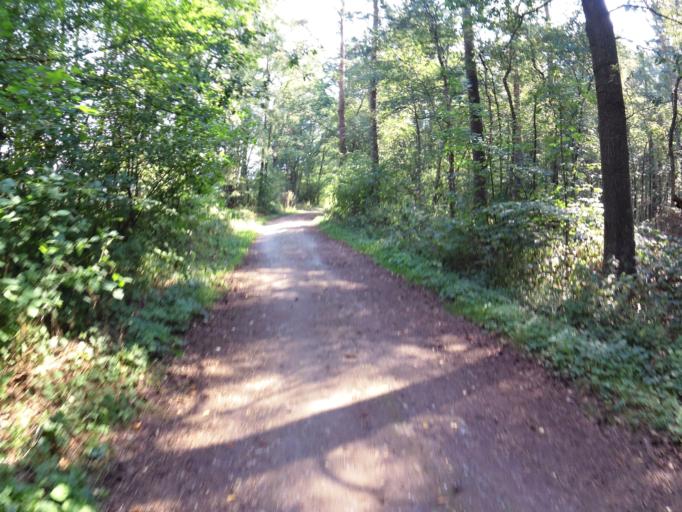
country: DE
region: North Rhine-Westphalia
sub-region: Regierungsbezirk Munster
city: Havixbeck
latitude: 51.9772
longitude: 7.4840
